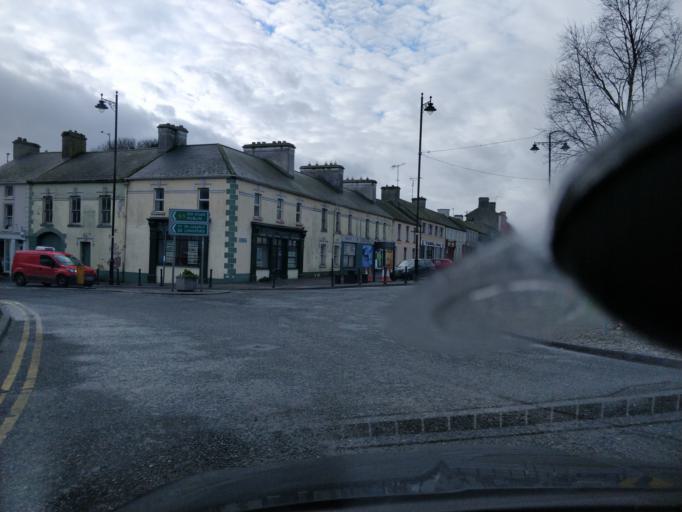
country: IE
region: Leinster
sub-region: An Longfort
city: Lanesborough
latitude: 53.7769
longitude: -8.1034
